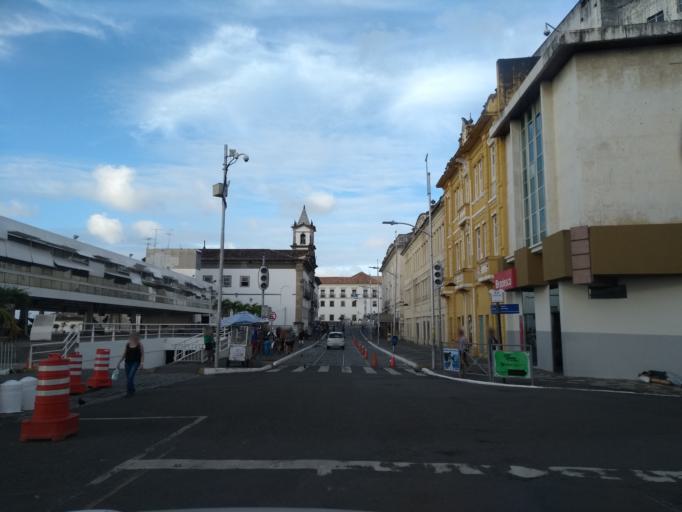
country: BR
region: Bahia
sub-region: Salvador
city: Salvador
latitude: -12.9747
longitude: -38.5125
